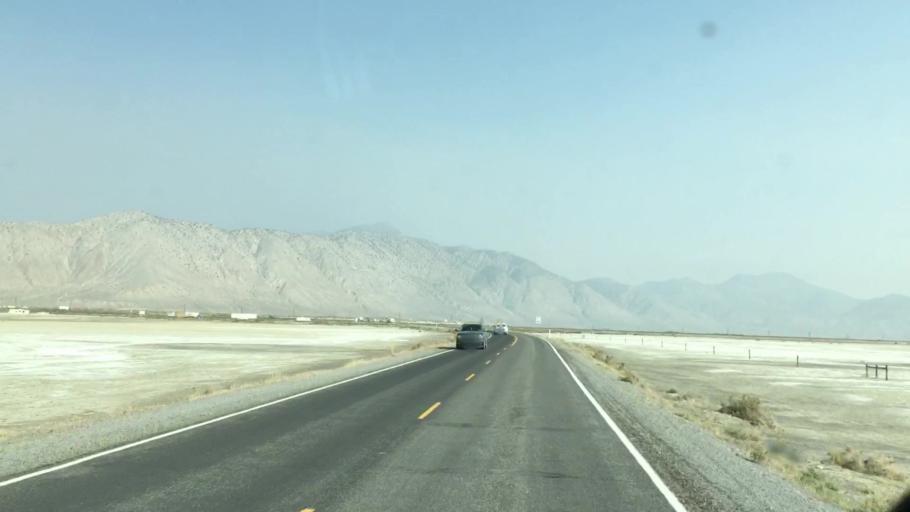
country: US
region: Nevada
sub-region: Pershing County
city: Lovelock
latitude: 40.6493
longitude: -119.3438
